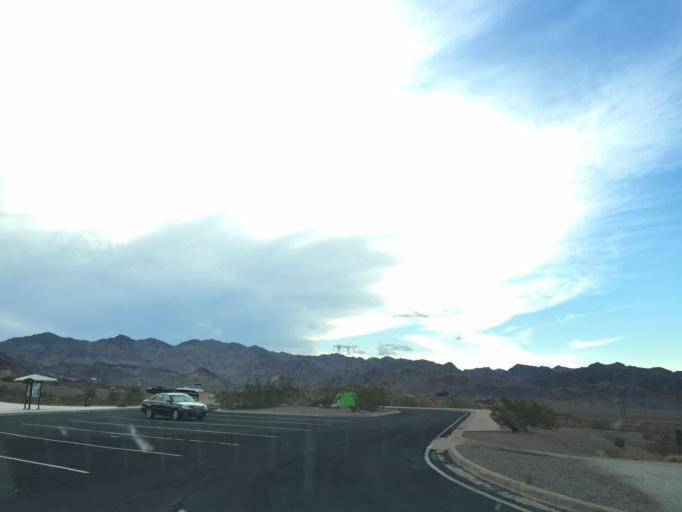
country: US
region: Nevada
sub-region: Clark County
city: Boulder City
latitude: 36.0118
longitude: -114.7932
